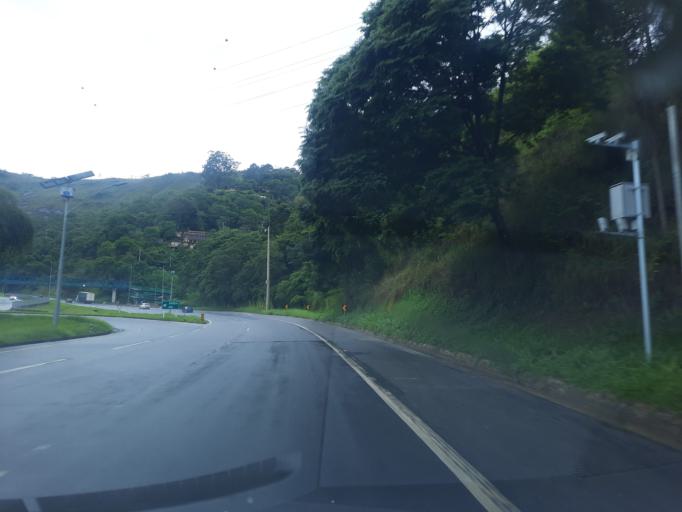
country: BR
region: Rio de Janeiro
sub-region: Petropolis
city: Petropolis
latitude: -22.4280
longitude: -43.1618
